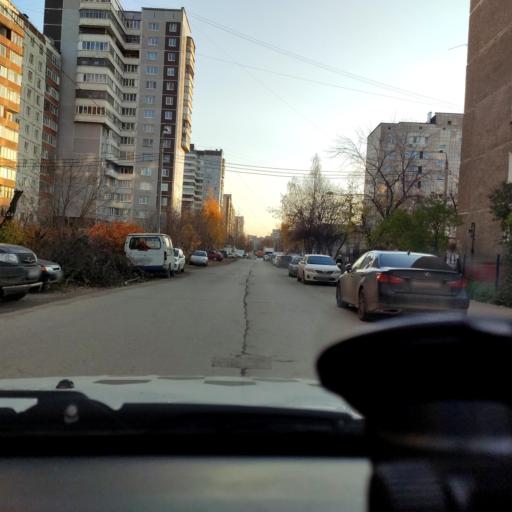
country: RU
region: Perm
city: Kondratovo
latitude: 57.9966
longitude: 56.1438
